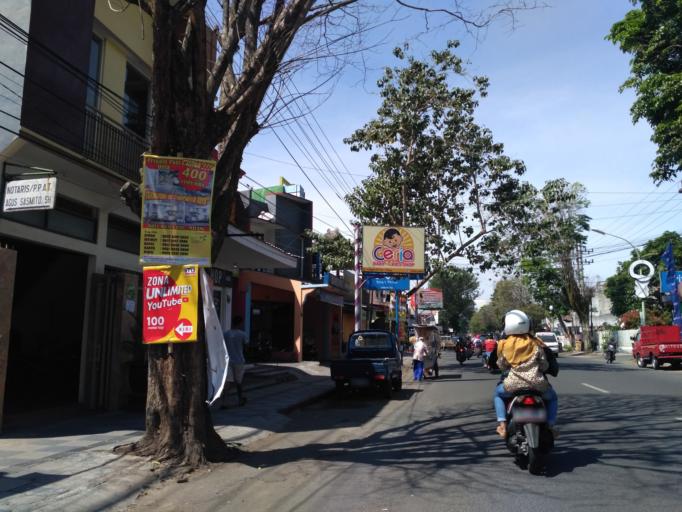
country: ID
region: East Java
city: Batu
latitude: -7.8742
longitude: 112.5300
